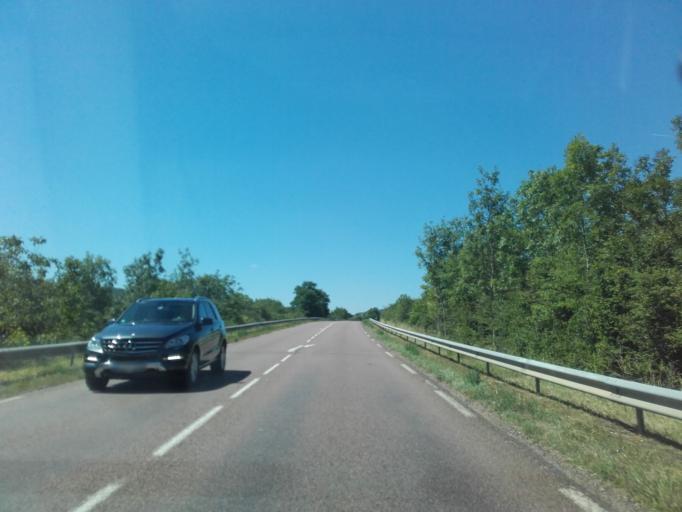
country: FR
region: Bourgogne
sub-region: Departement de Saone-et-Loire
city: Chagny
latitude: 46.9168
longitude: 4.7274
